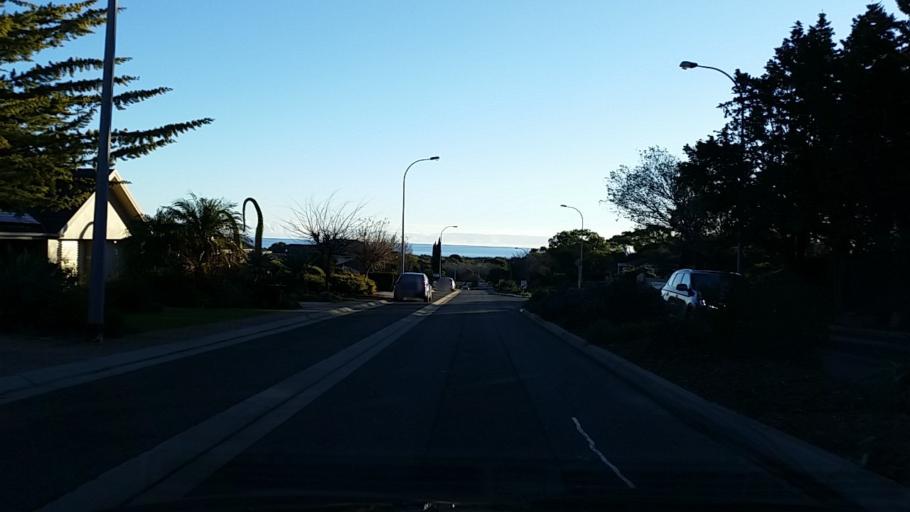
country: AU
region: South Australia
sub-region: Onkaparinga
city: Moana
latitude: -35.2016
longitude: 138.4828
